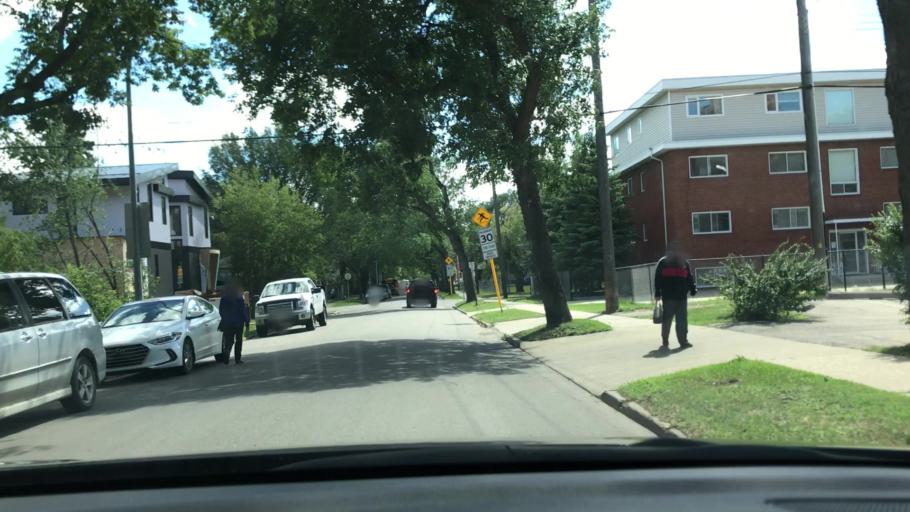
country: CA
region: Alberta
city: Edmonton
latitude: 53.5225
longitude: -113.4887
